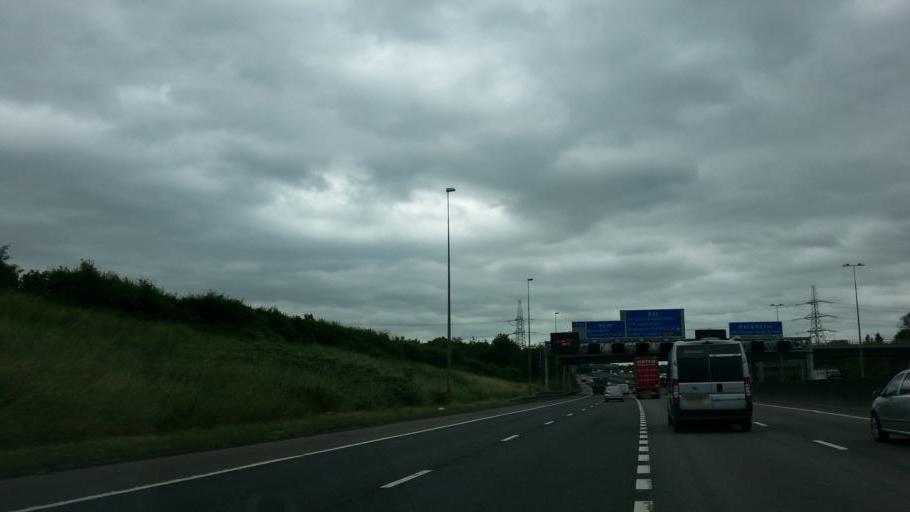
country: GB
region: England
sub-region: Warwickshire
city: Curdworth
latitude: 52.5302
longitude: -1.7292
